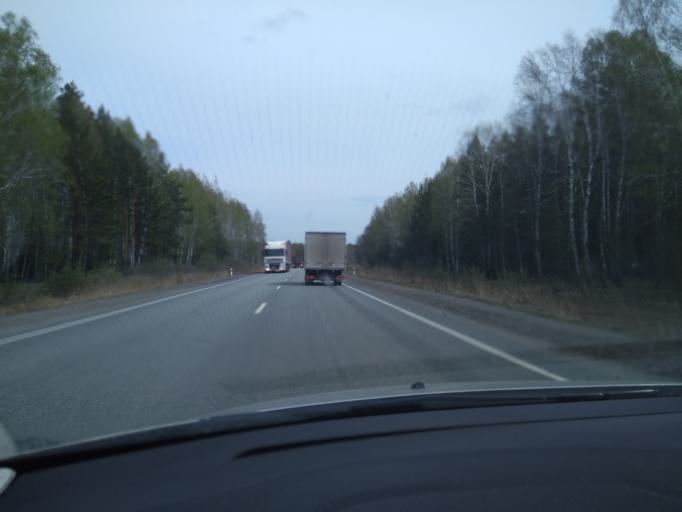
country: RU
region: Sverdlovsk
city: Yushala
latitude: 57.1134
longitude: 64.2394
